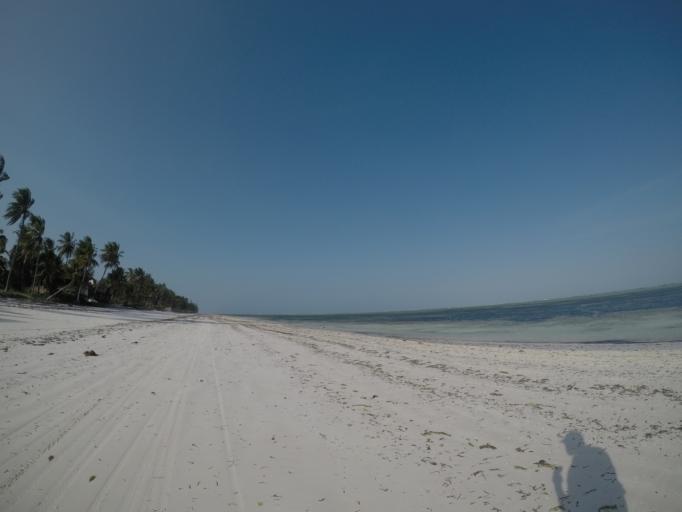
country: TZ
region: Zanzibar Central/South
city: Nganane
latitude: -6.2042
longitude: 39.5352
